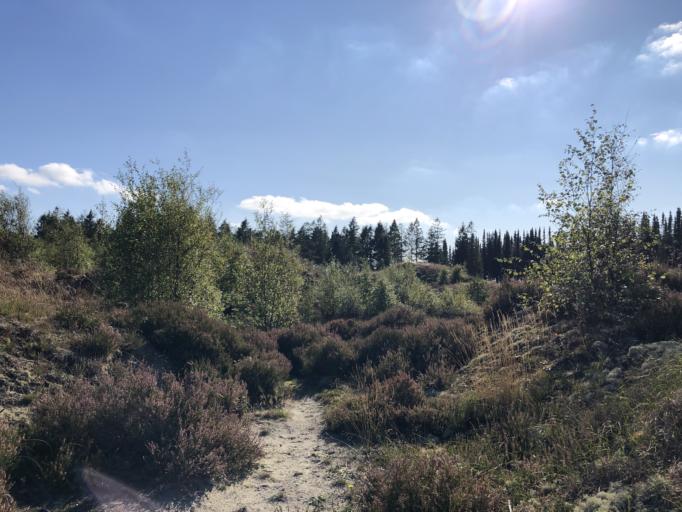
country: DK
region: Central Jutland
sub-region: Holstebro Kommune
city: Holstebro
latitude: 56.2481
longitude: 8.4918
